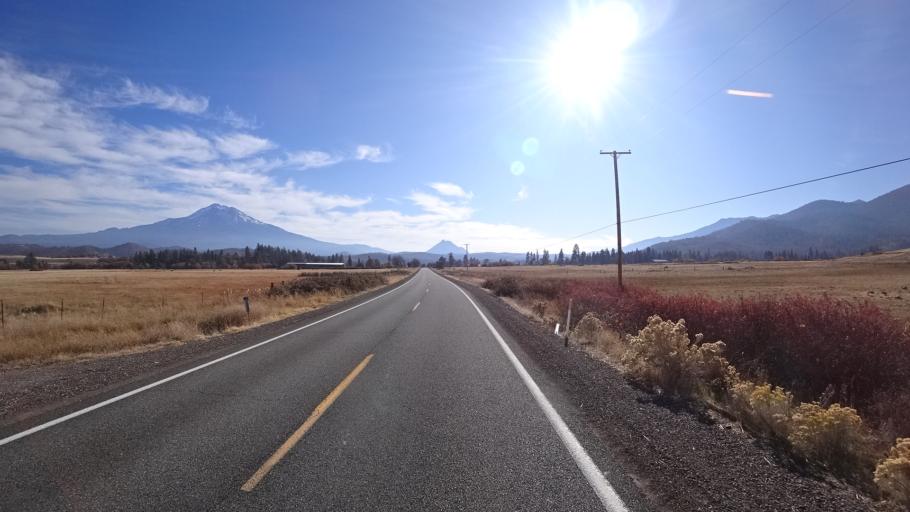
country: US
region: California
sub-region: Siskiyou County
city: Weed
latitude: 41.4527
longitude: -122.4570
